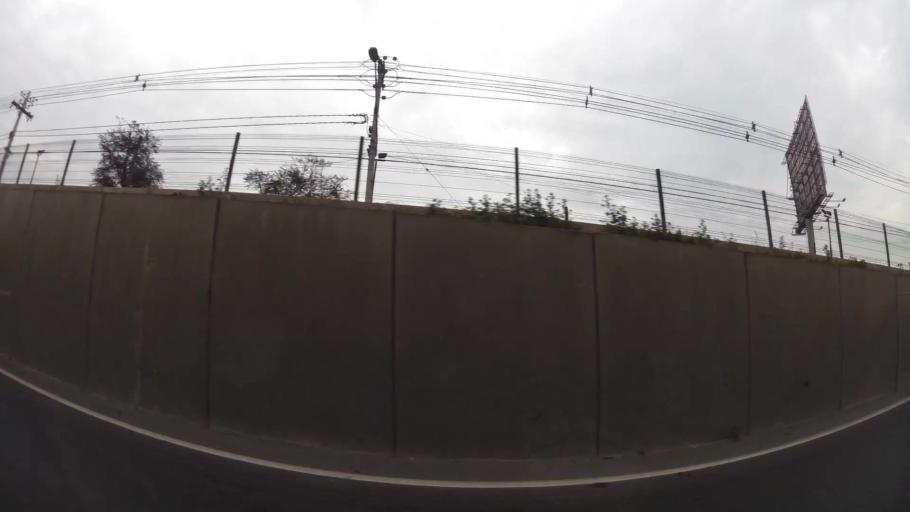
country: CL
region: Santiago Metropolitan
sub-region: Provincia de Santiago
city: Lo Prado
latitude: -33.4691
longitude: -70.7617
